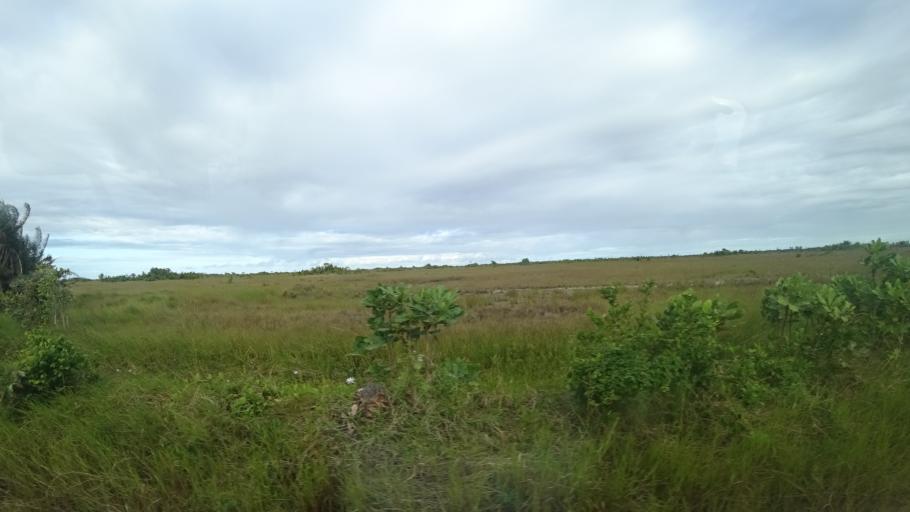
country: MZ
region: Sofala
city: Beira
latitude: -19.6977
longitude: 35.0309
